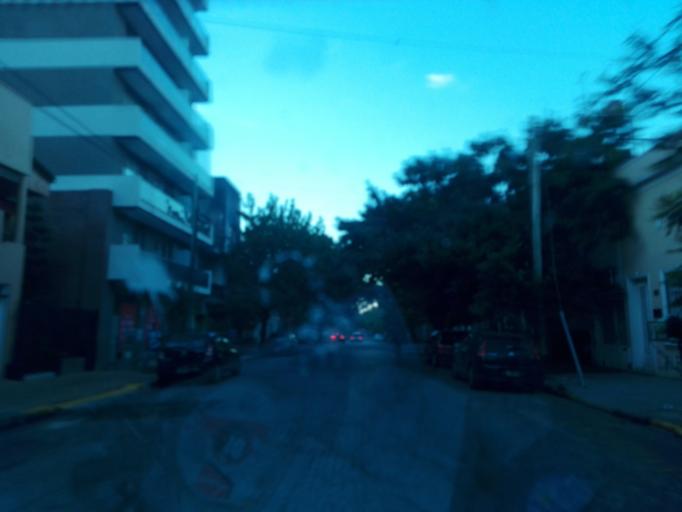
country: AR
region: Buenos Aires
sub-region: Partido de La Plata
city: La Plata
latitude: -34.9091
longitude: -57.9505
